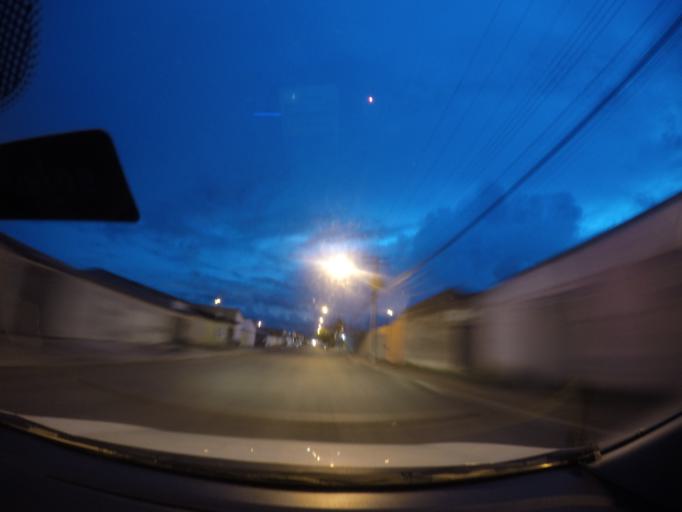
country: BR
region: Goias
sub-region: Goiania
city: Goiania
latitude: -16.7255
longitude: -49.3673
